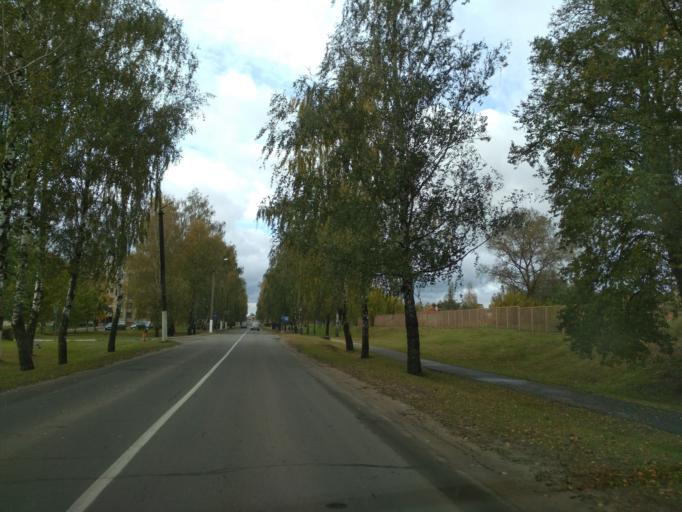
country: BY
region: Minsk
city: Mar''ina Horka
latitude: 53.5049
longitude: 28.1655
